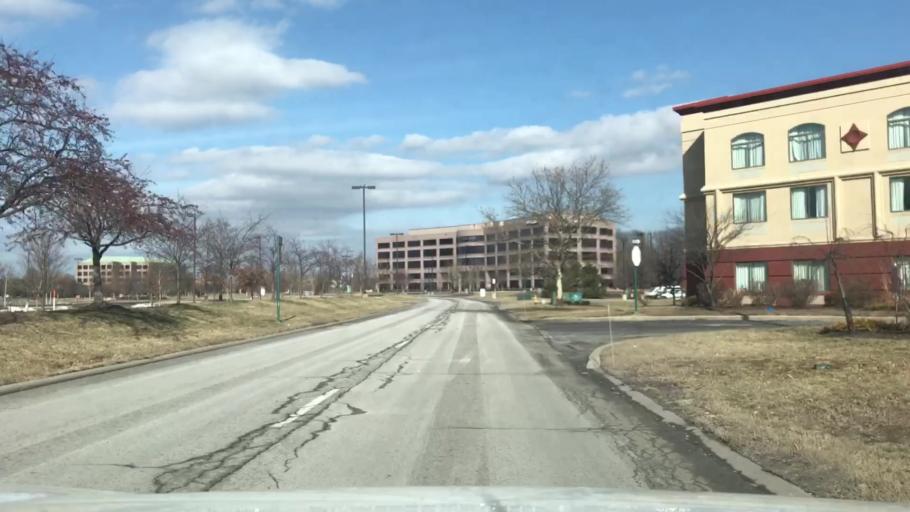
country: US
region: Missouri
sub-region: Saint Charles County
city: Saint Charles
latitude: 38.7512
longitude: -90.4642
